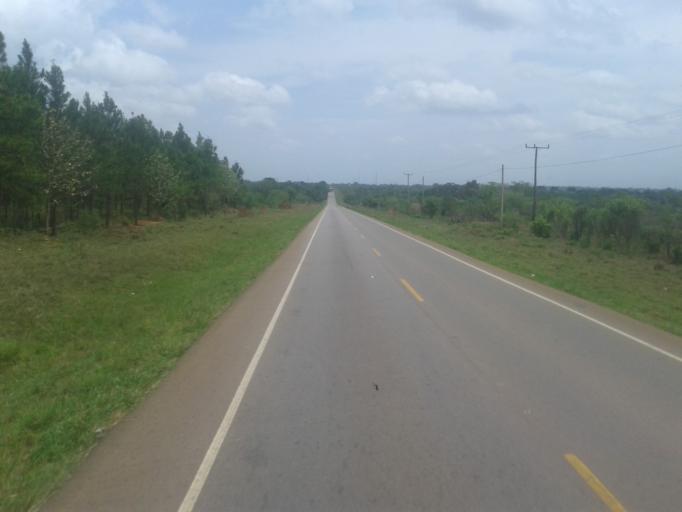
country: UG
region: Central Region
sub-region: Nakasongola District
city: Nakasongola
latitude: 1.4034
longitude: 32.2936
